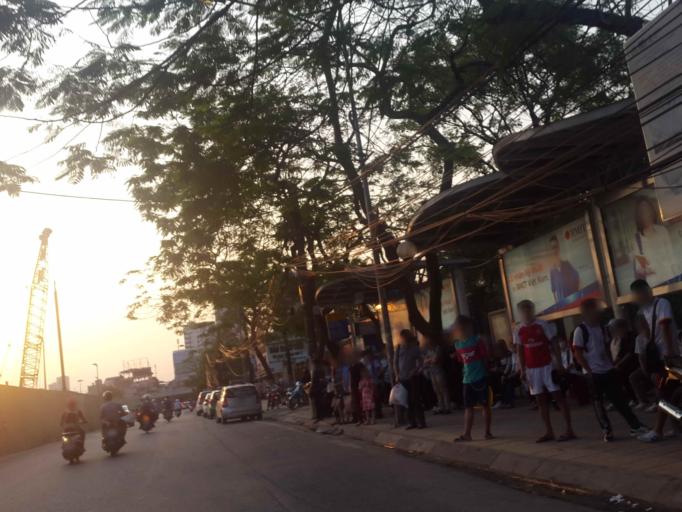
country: VN
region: Ha Noi
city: Cau Giay
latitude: 21.0291
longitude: 105.8040
